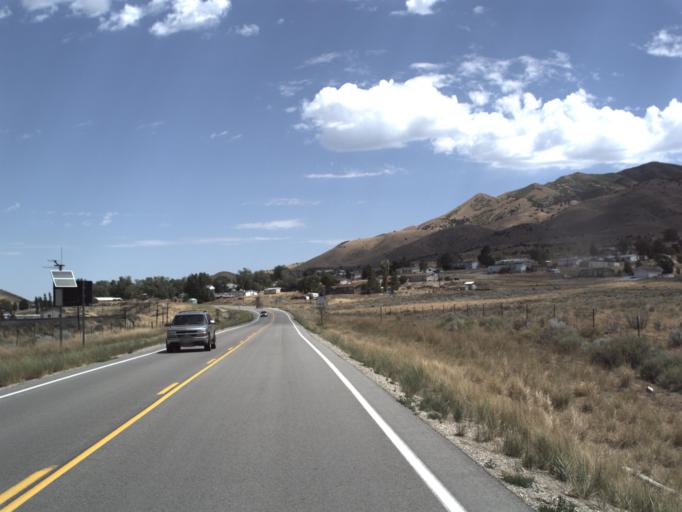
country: US
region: Utah
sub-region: Tooele County
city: Tooele
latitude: 40.4420
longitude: -112.3686
